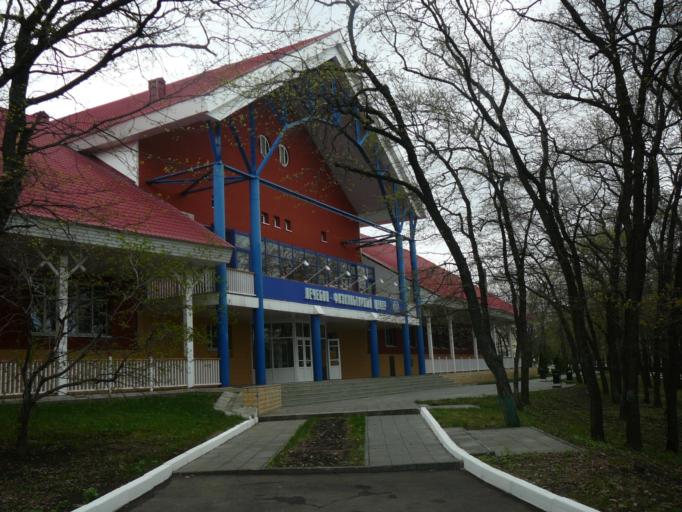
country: RU
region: Saratov
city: Shumeyka
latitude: 51.5947
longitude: 46.1838
